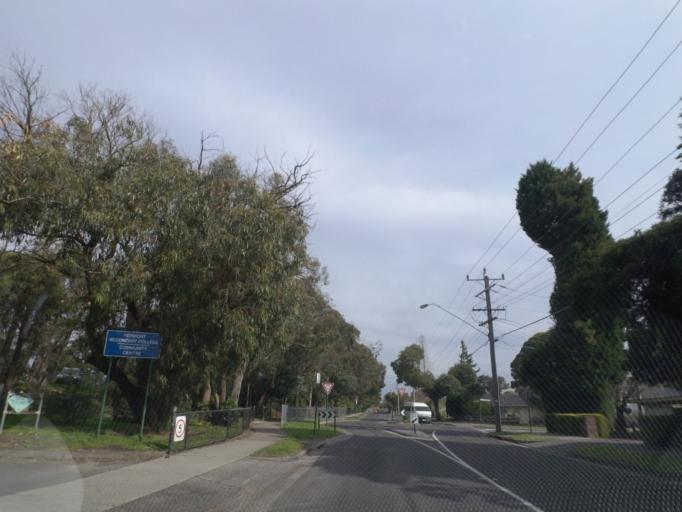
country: AU
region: Victoria
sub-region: Whitehorse
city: Vermont
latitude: -37.8440
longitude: 145.1995
